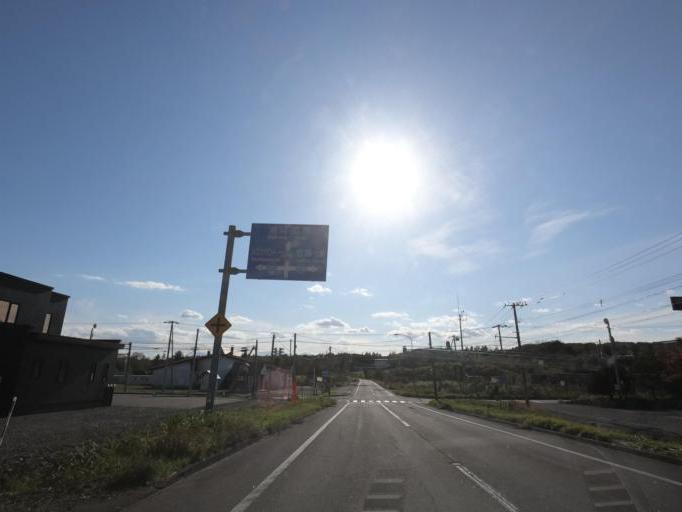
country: JP
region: Hokkaido
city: Obihiro
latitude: 42.5993
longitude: 143.4521
